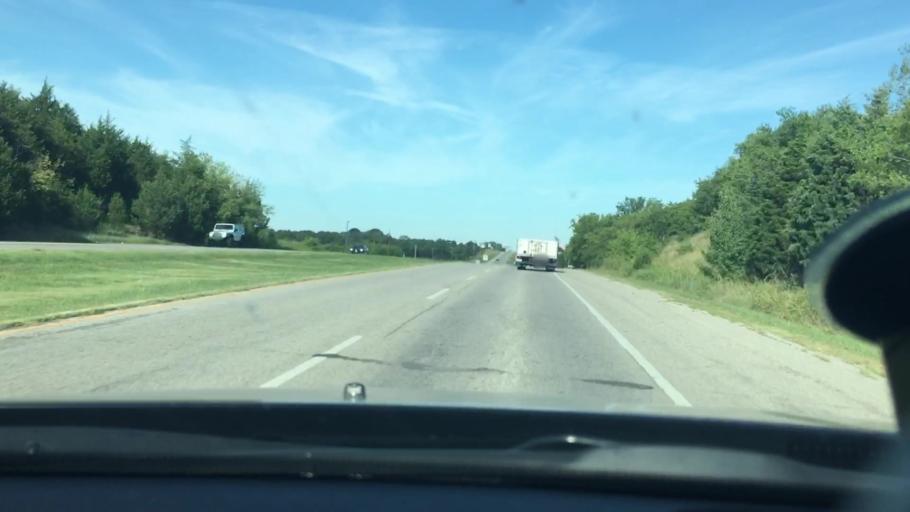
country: US
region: Oklahoma
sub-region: Carter County
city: Ardmore
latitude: 34.1730
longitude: -97.1979
